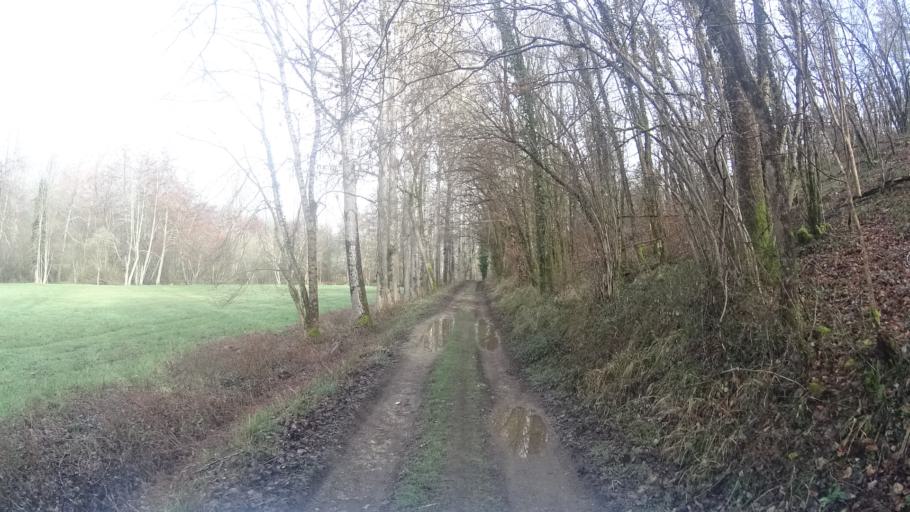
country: FR
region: Aquitaine
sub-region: Departement de la Dordogne
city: Terrasson-Lavilledieu
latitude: 45.0957
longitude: 1.2634
